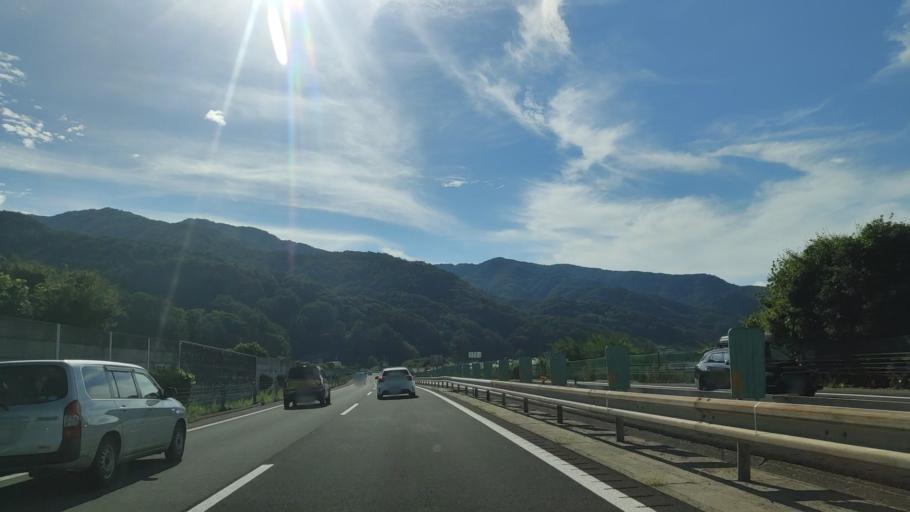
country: JP
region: Nagano
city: Suwa
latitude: 36.0041
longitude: 138.1165
